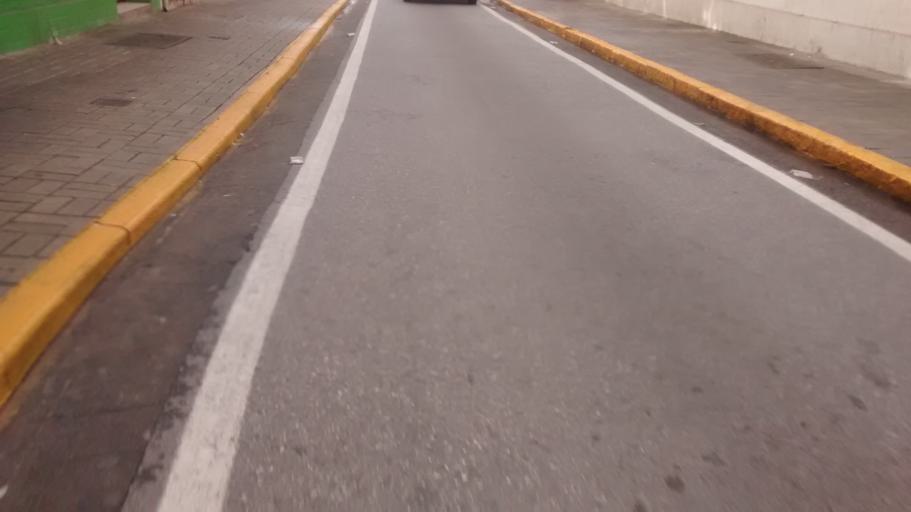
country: BR
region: Minas Gerais
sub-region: Itajuba
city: Itajuba
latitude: -22.4237
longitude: -45.4528
